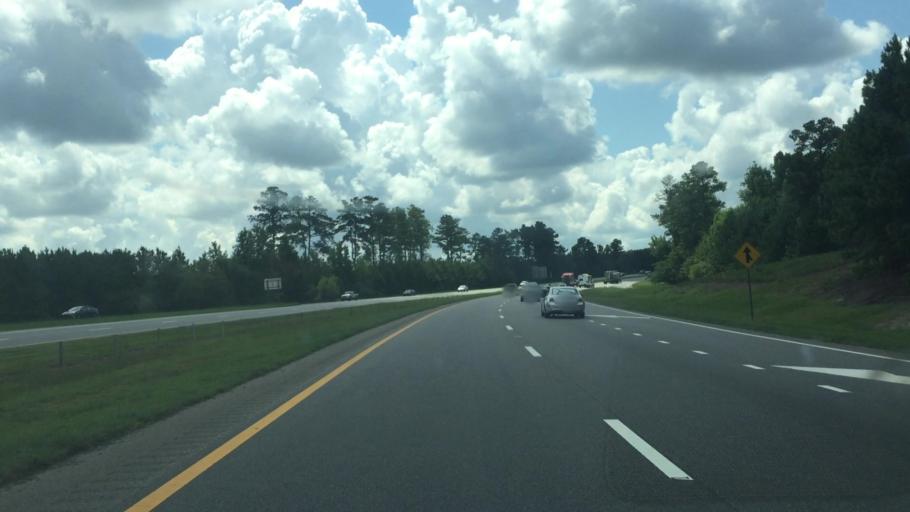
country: US
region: North Carolina
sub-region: Richmond County
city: East Rockingham
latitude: 34.9094
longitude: -79.7911
